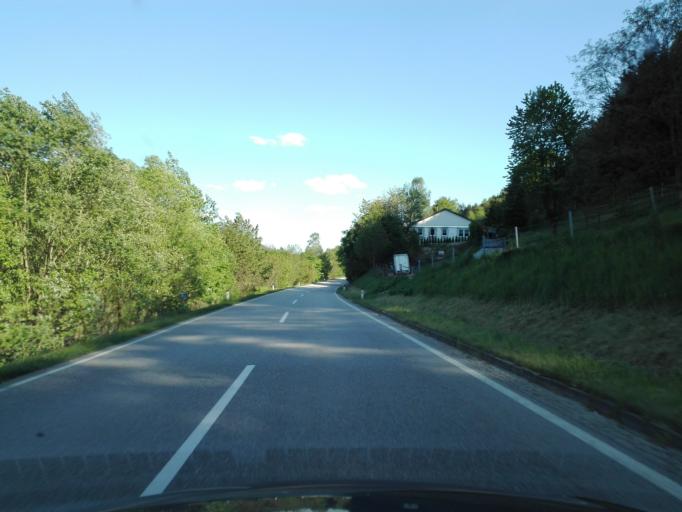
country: AT
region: Upper Austria
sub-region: Politischer Bezirk Rohrbach
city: Pfarrkirchen im Muehlkreis
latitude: 48.4839
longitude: 13.7522
